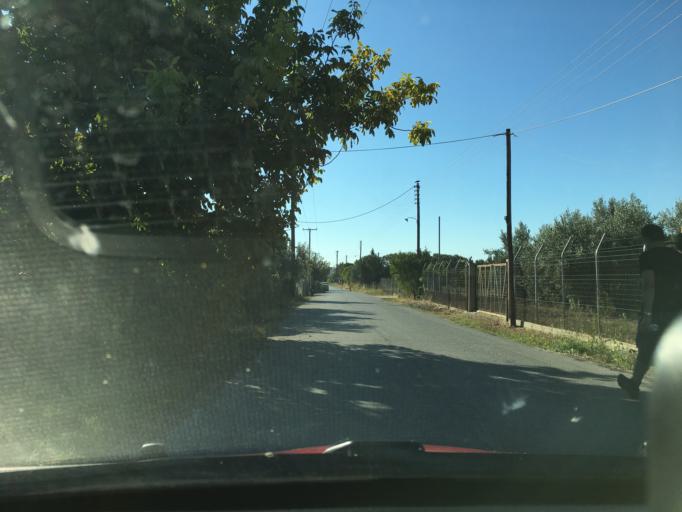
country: GR
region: Central Macedonia
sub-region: Nomos Chalkidikis
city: Nea Poteidaia
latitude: 40.2045
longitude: 23.3238
